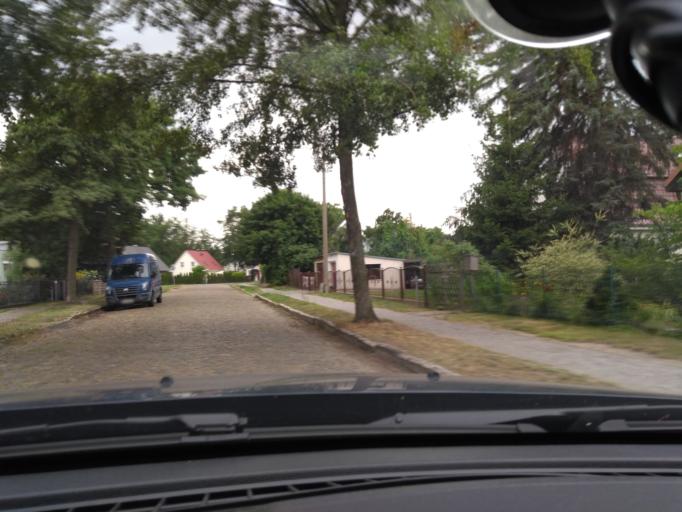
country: DE
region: Brandenburg
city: Dallgow-Doeberitz
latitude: 52.5556
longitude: 13.0721
